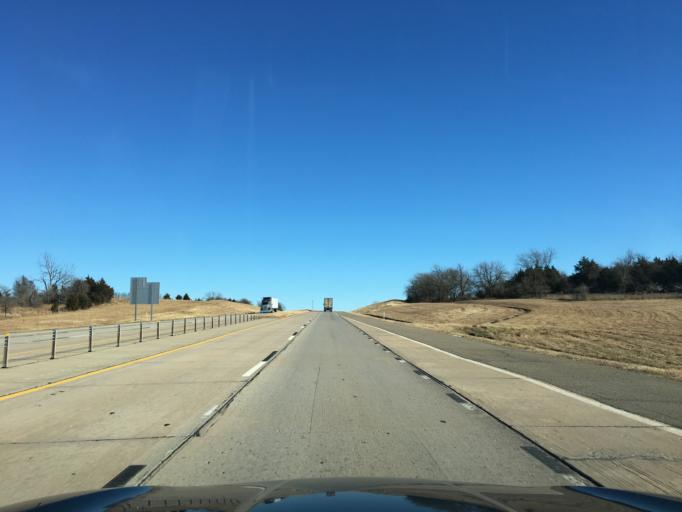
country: US
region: Oklahoma
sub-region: Pawnee County
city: Pawnee
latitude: 36.2248
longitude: -96.7770
